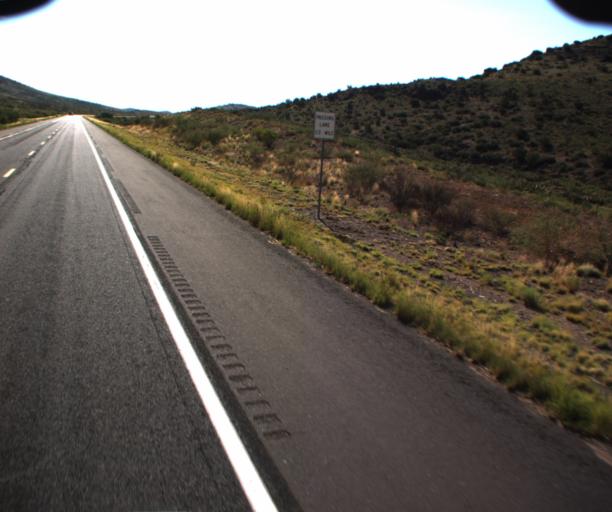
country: US
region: Arizona
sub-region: Greenlee County
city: Clifton
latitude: 32.8516
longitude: -109.3298
